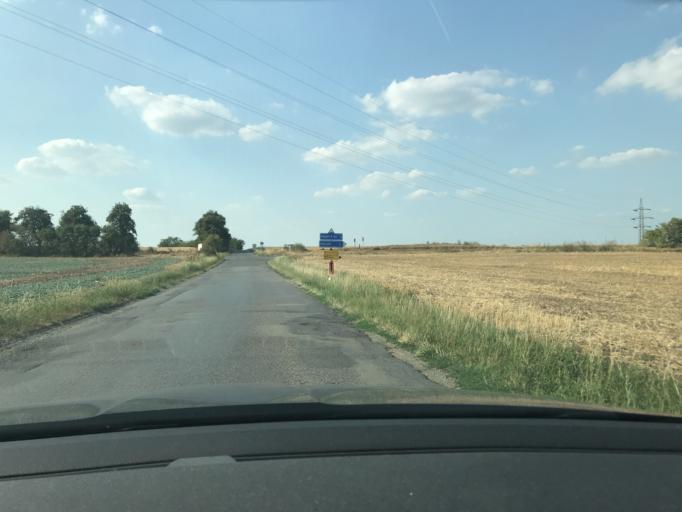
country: CZ
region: Central Bohemia
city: Kralupy nad Vltavou
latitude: 50.2259
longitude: 14.3217
